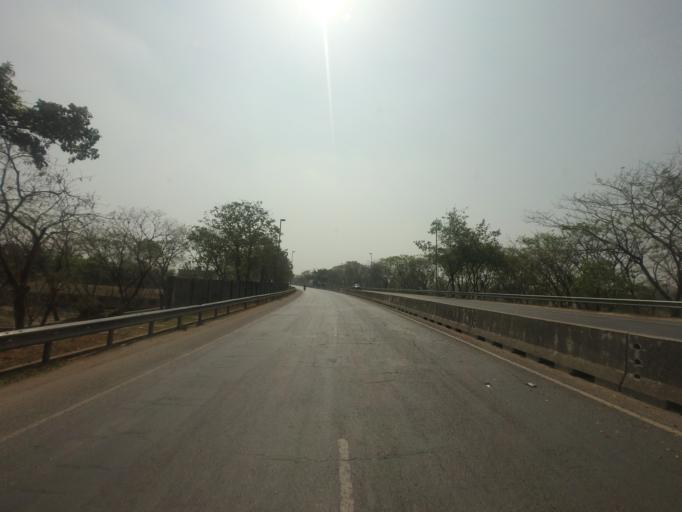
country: BD
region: Dhaka
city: Bhairab Bazar
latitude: 24.0505
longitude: 90.9904
